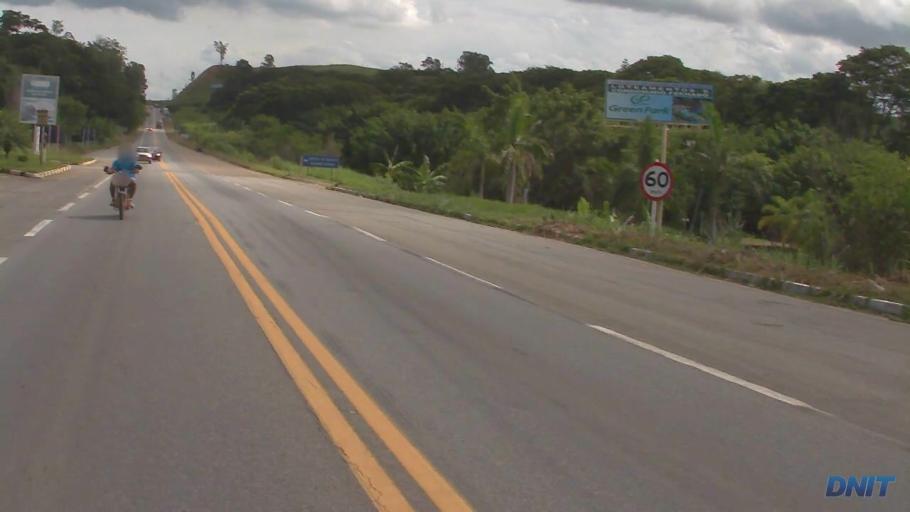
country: BR
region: Minas Gerais
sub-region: Ipatinga
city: Ipatinga
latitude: -19.4398
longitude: -42.5114
